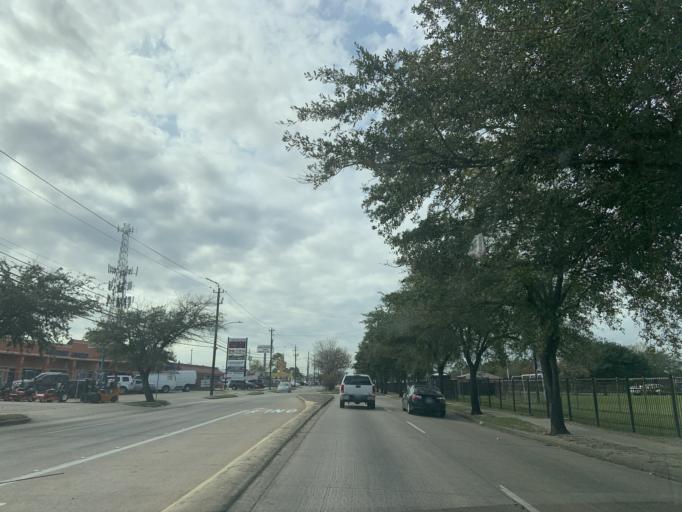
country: US
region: Texas
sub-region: Harris County
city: Bellaire
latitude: 29.6939
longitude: -95.4950
